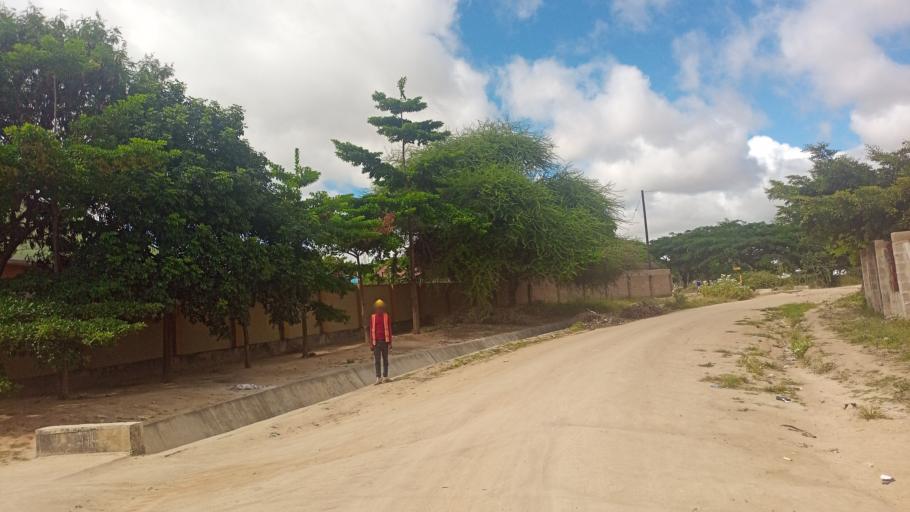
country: TZ
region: Dodoma
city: Dodoma
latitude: -6.1925
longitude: 35.7350
